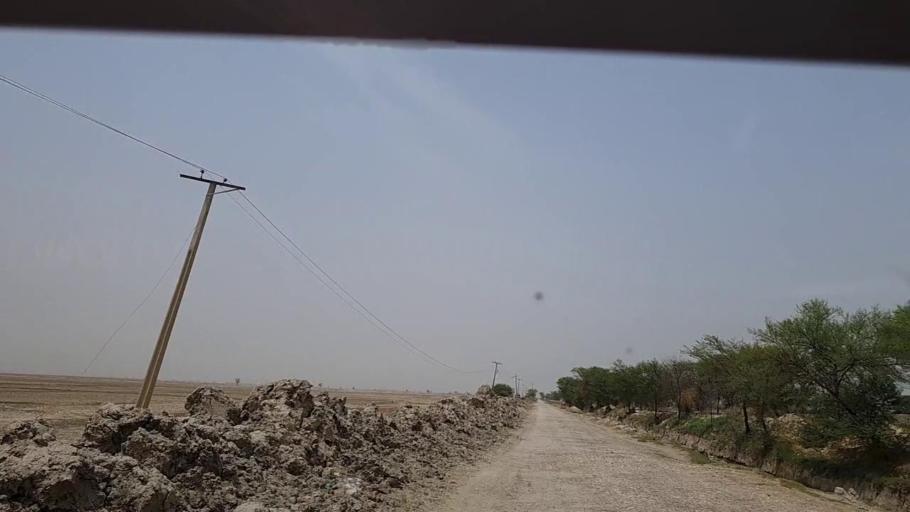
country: PK
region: Sindh
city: Khairpur Nathan Shah
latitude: 27.0441
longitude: 67.6188
